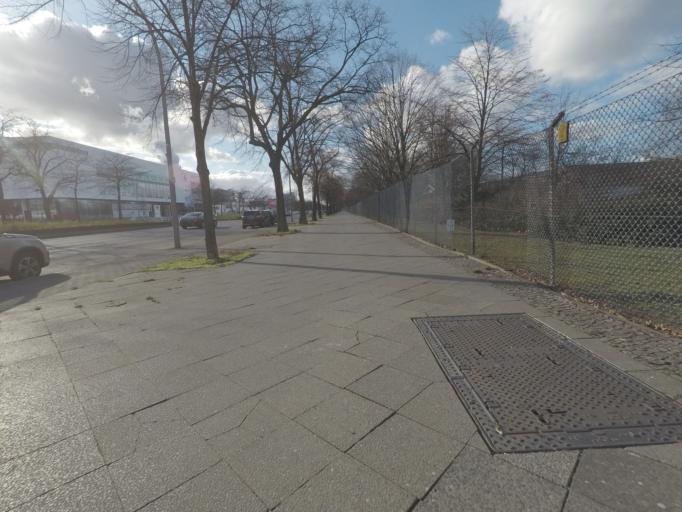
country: DE
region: Berlin
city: Siemensstadt
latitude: 52.5374
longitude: 13.2595
